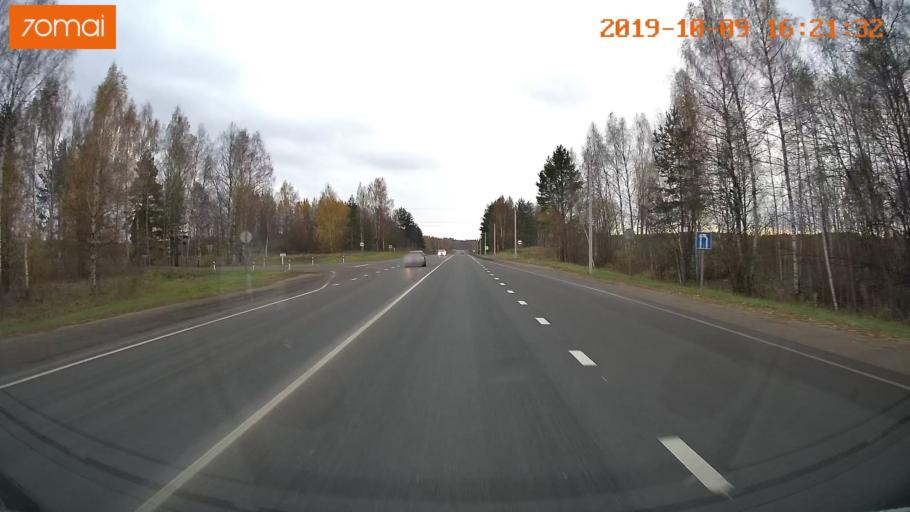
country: RU
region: Kostroma
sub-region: Kostromskoy Rayon
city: Kostroma
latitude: 57.6905
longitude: 40.8888
